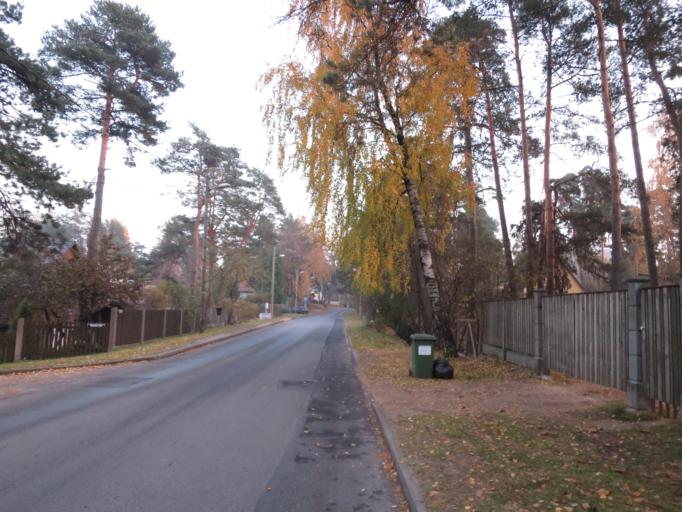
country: LV
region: Riga
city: Bergi
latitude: 56.9882
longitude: 24.2932
